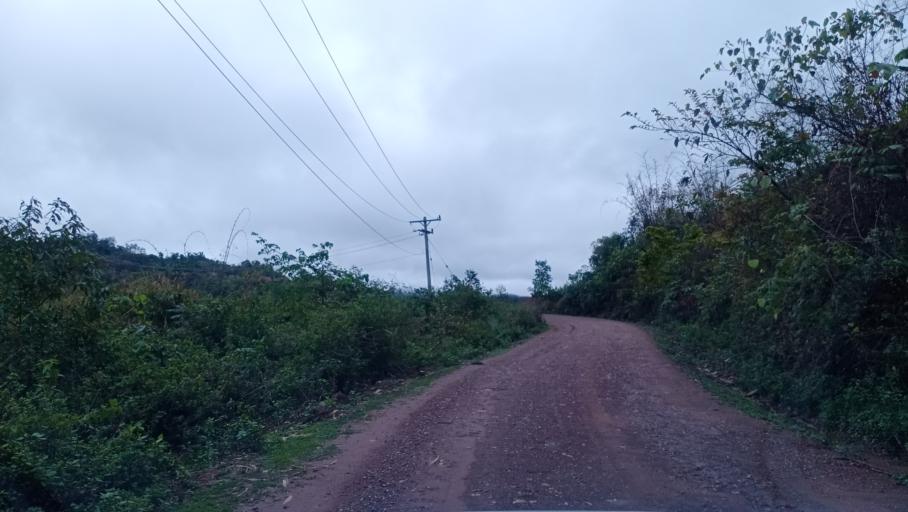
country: LA
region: Phongsali
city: Phongsali
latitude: 21.3424
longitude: 102.0872
